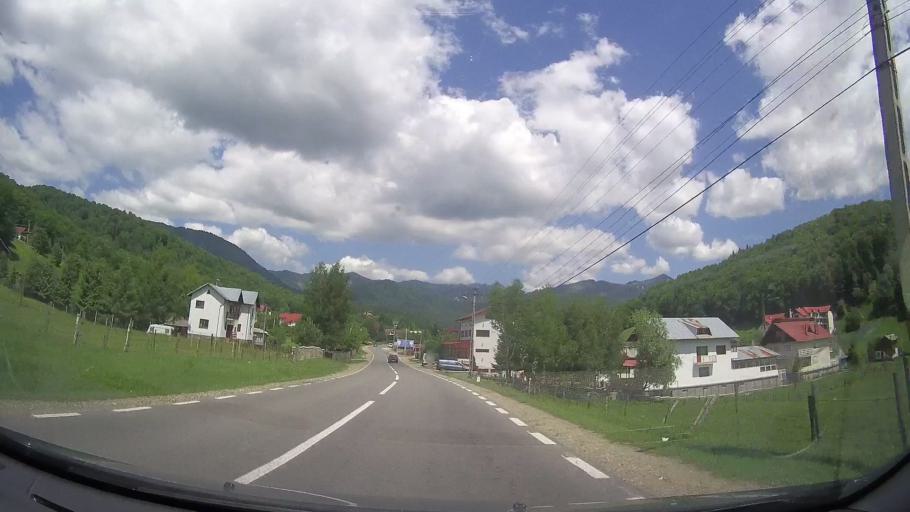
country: RO
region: Prahova
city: Maneciu
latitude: 45.4437
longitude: 25.9381
